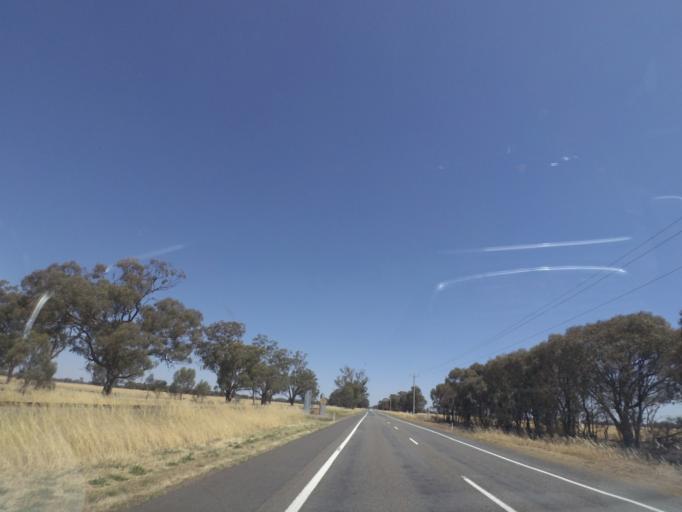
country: AU
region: Victoria
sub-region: Greater Shepparton
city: Shepparton
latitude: -36.2008
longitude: 145.4318
